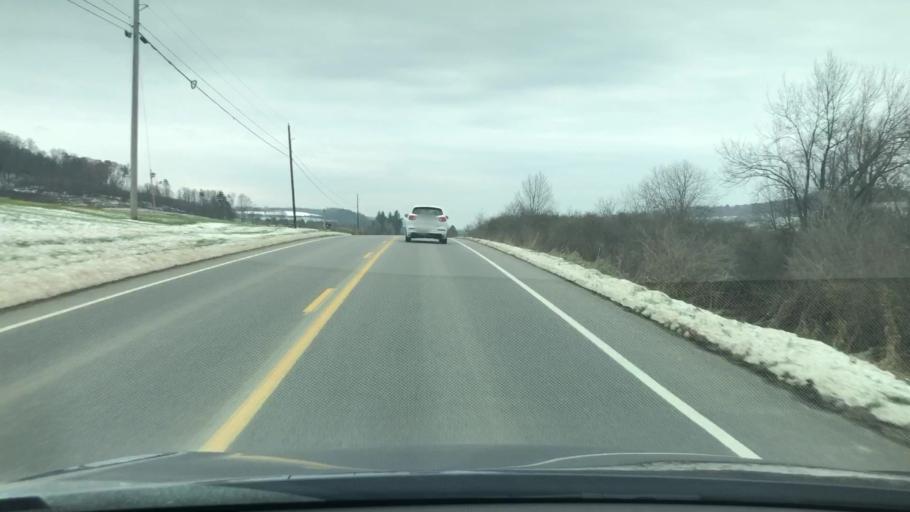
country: US
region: Pennsylvania
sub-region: Jefferson County
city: Brookville
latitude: 41.1010
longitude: -79.2212
